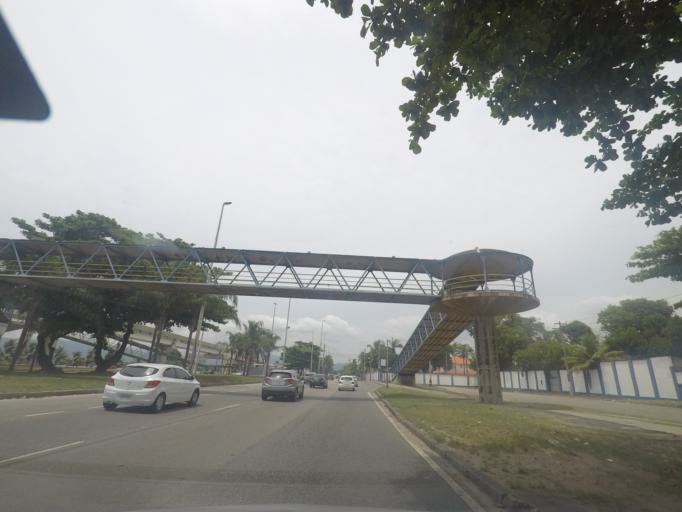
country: BR
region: Rio de Janeiro
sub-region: Rio De Janeiro
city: Rio de Janeiro
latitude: -22.8248
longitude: -43.2325
